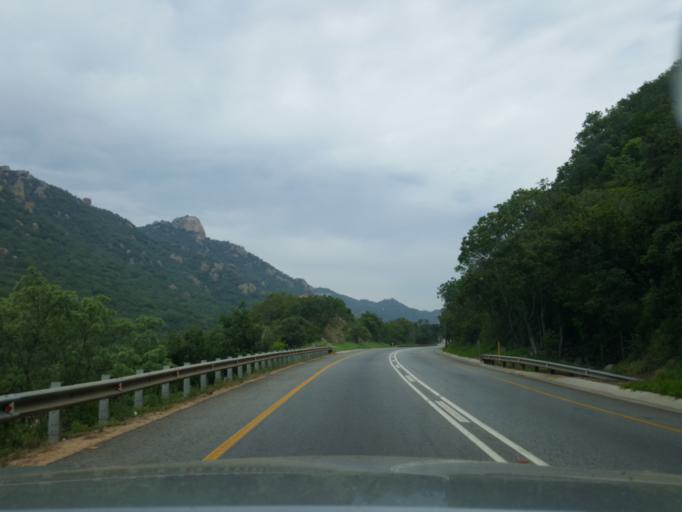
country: ZA
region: Mpumalanga
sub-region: Ehlanzeni District
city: Nelspruit
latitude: -25.5119
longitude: 31.2166
